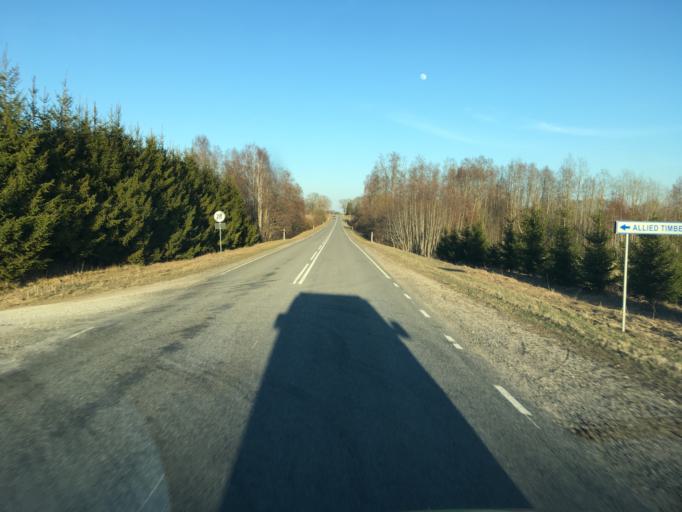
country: EE
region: Raplamaa
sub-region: Rapla vald
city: Rapla
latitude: 59.0798
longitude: 24.8350
